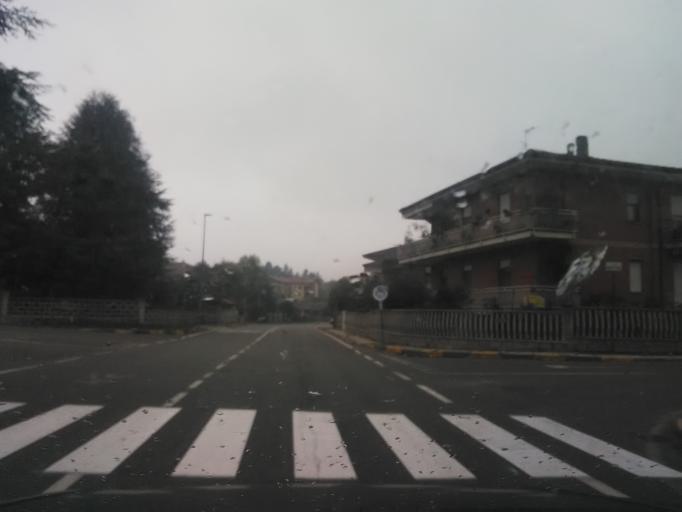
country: IT
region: Piedmont
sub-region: Provincia di Biella
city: Cavaglia
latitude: 45.4085
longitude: 8.0936
